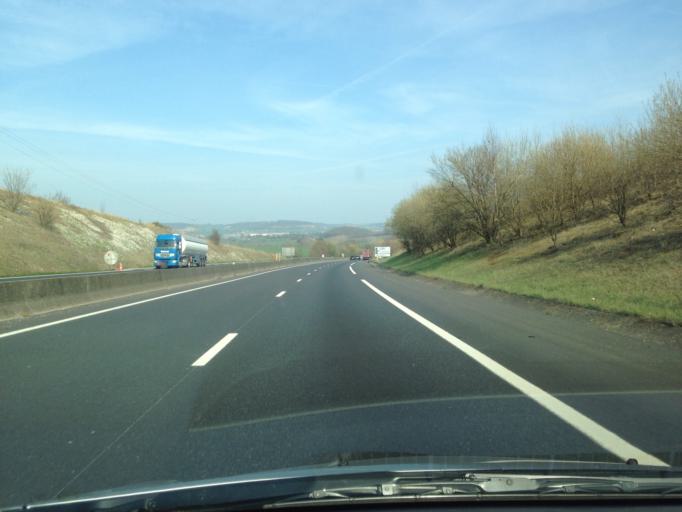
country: FR
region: Haute-Normandie
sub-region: Departement de la Seine-Maritime
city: Mesnieres-en-Bray
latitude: 49.7118
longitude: 1.3856
